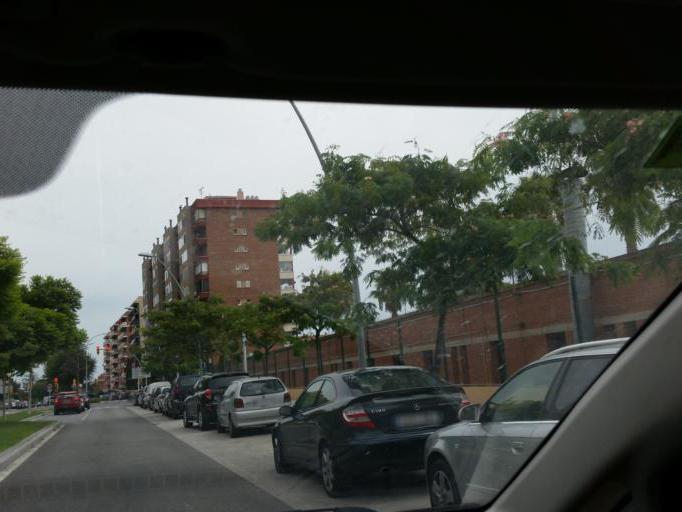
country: ES
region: Catalonia
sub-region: Provincia de Barcelona
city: Vilassar de Mar
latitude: 41.5054
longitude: 2.3860
